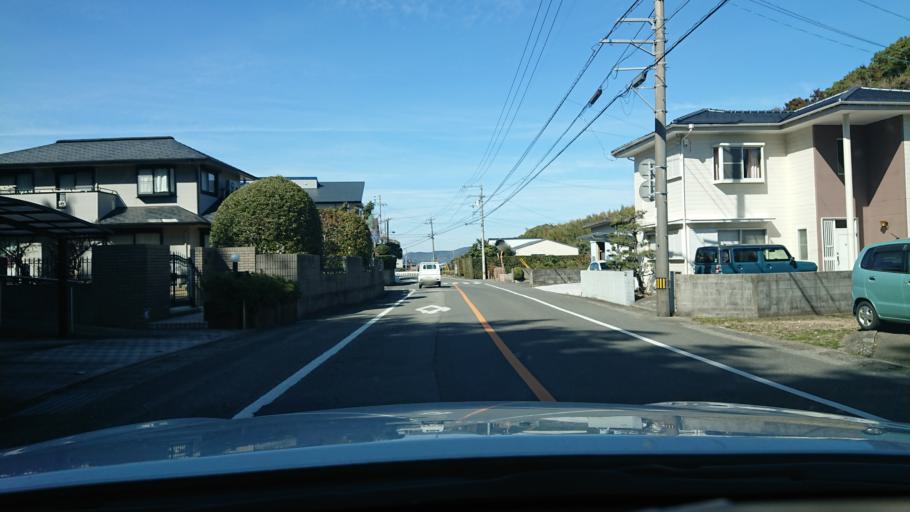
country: JP
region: Tokushima
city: Komatsushimacho
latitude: 33.9743
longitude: 134.5908
